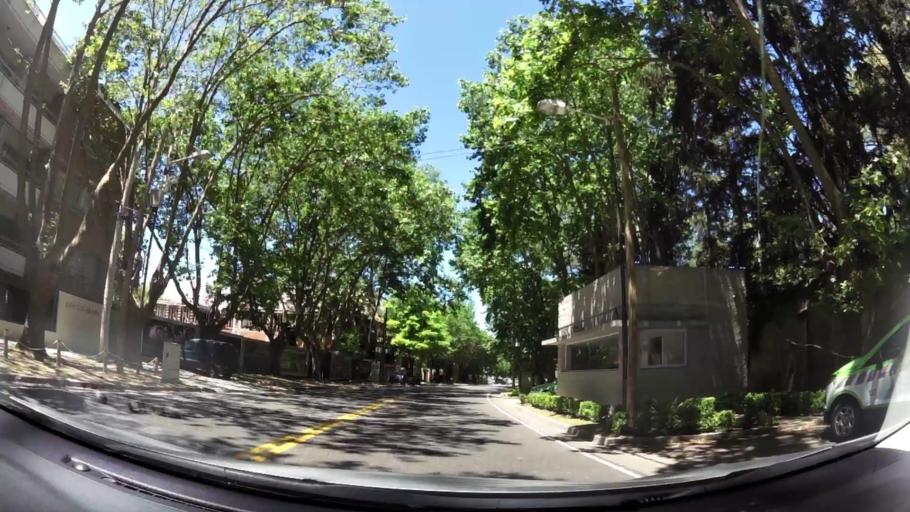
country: AR
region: Buenos Aires
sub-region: Partido de San Isidro
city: San Isidro
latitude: -34.4507
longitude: -58.5310
